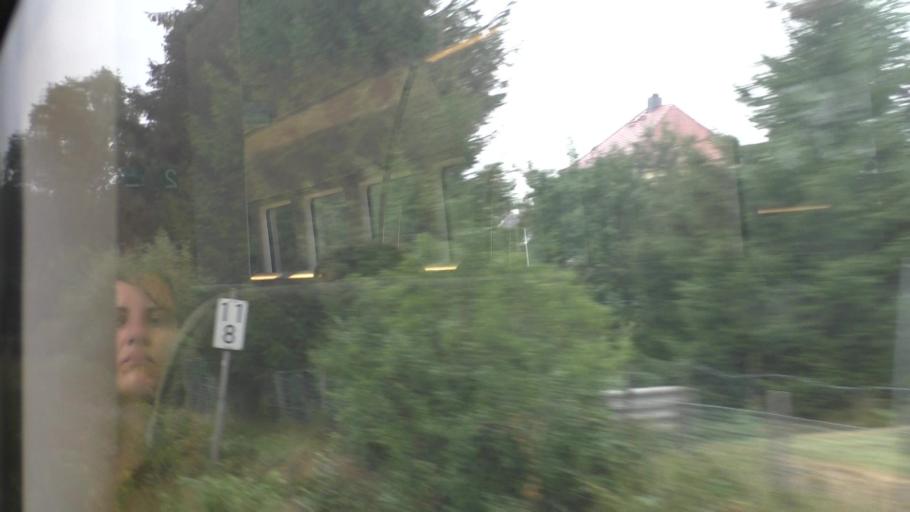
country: DE
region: Saxony
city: Ebersbach
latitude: 50.9913
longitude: 14.5868
